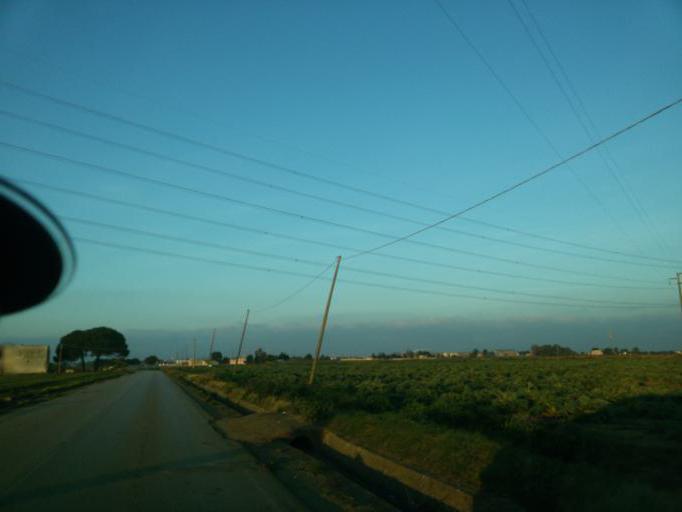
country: IT
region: Apulia
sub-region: Provincia di Brindisi
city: La Rosa
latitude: 40.5920
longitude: 17.9446
